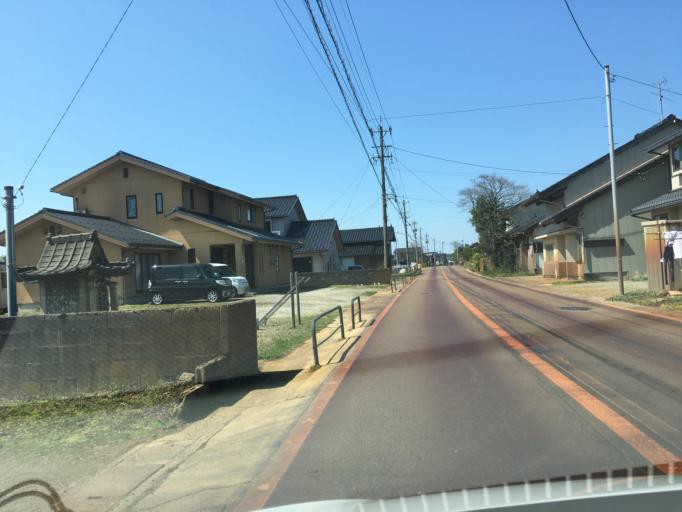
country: JP
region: Toyama
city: Kuragaki-kosugi
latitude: 36.7568
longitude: 137.1836
